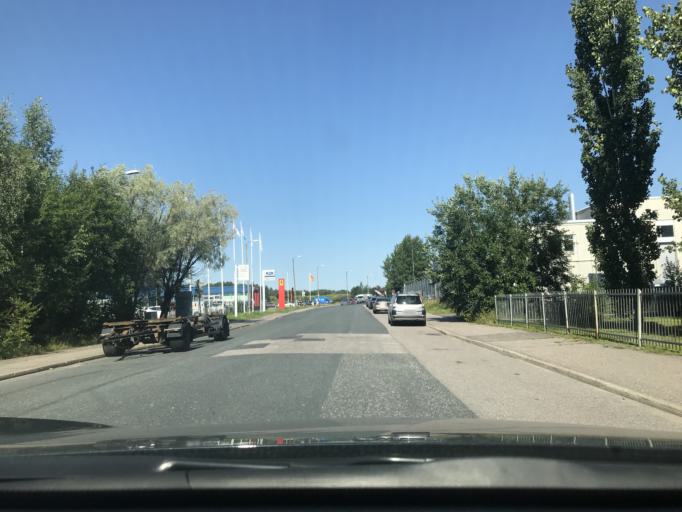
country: FI
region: Uusimaa
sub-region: Helsinki
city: Vantaa
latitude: 60.2433
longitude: 25.0468
